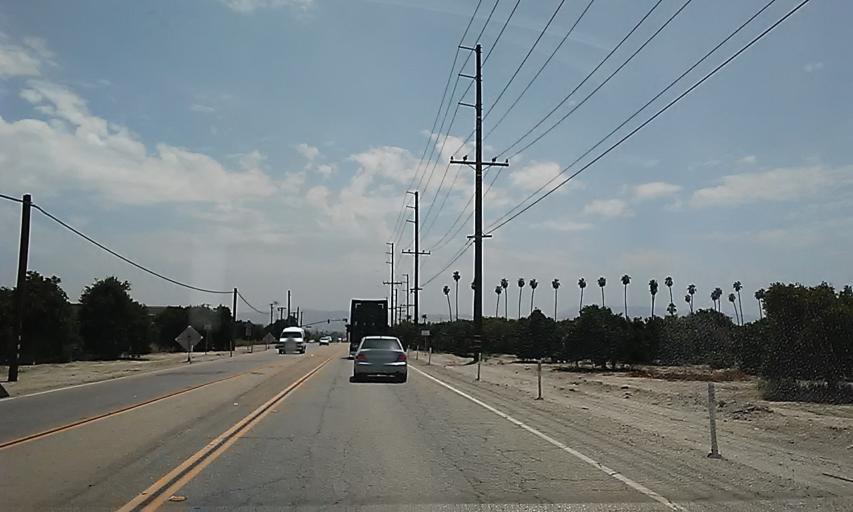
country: US
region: California
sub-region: San Bernardino County
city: Redlands
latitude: 34.0837
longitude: -117.2088
